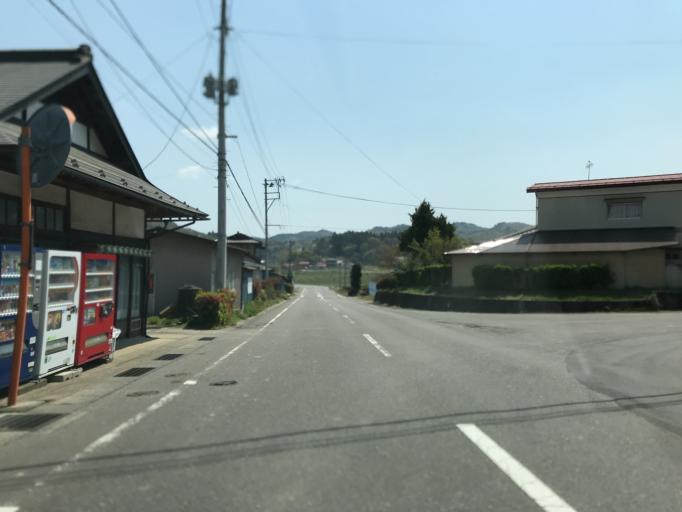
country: JP
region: Fukushima
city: Ishikawa
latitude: 37.0707
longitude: 140.4242
